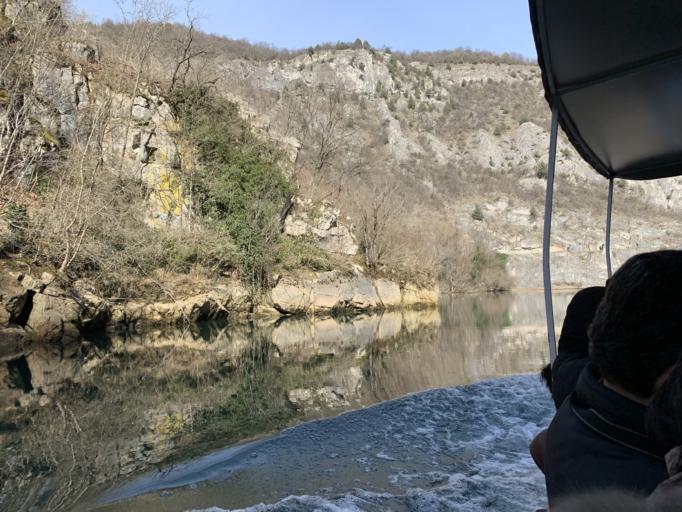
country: MK
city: Grchec
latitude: 41.9325
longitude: 21.2955
